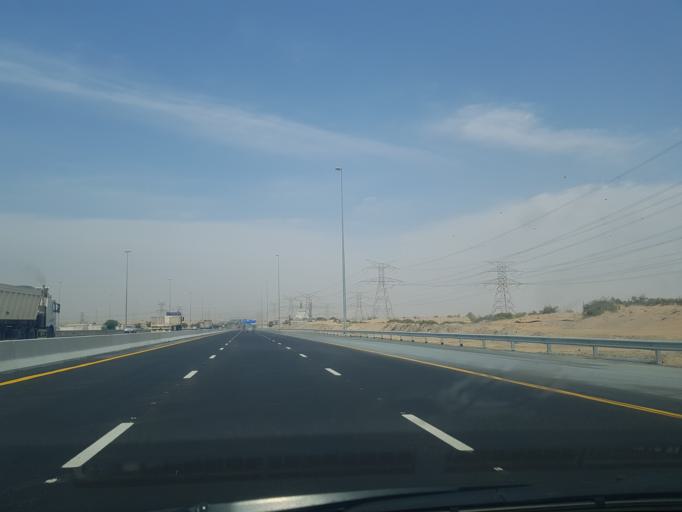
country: AE
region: Ash Shariqah
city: Sharjah
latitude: 25.2234
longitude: 55.5597
